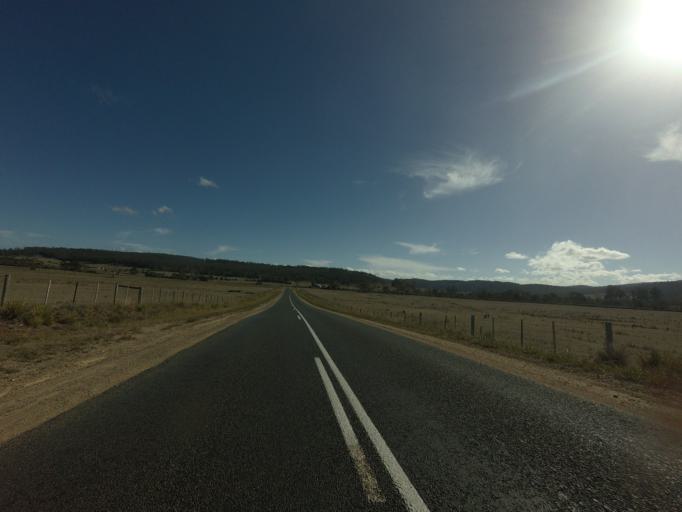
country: AU
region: Tasmania
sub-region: Break O'Day
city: St Helens
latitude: -41.9519
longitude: 148.1889
